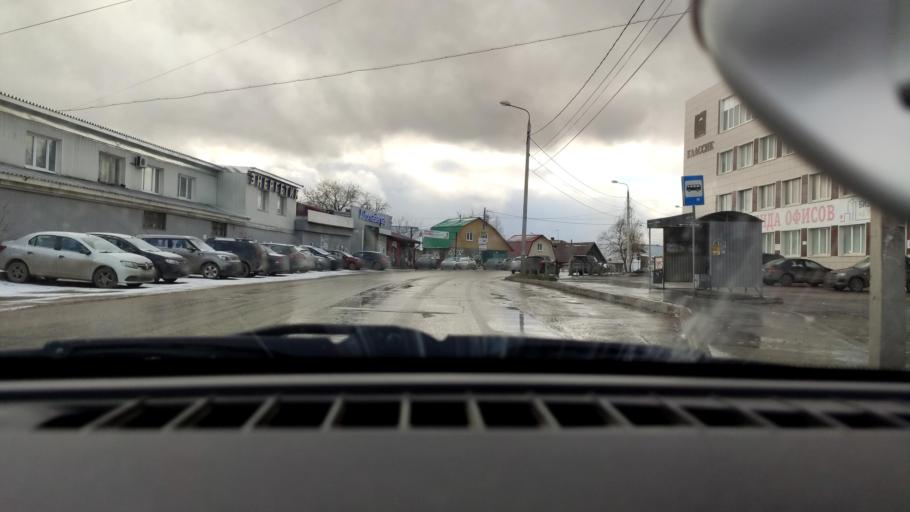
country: RU
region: Perm
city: Perm
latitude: 57.9780
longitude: 56.2687
